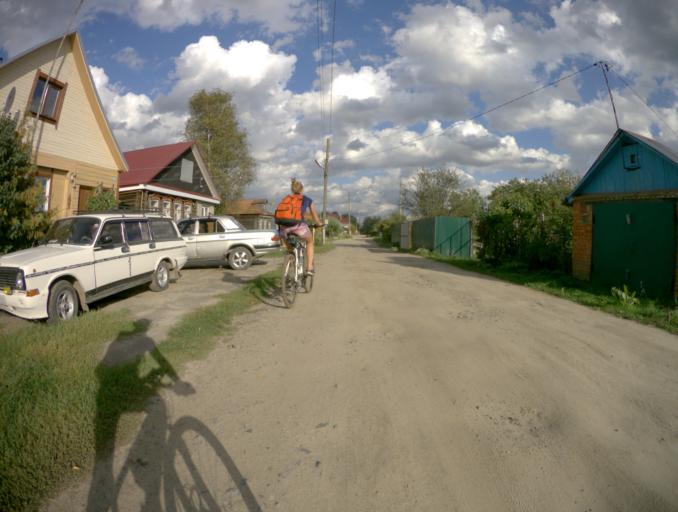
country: RU
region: Vladimir
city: Raduzhnyy
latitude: 56.0280
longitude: 40.2843
